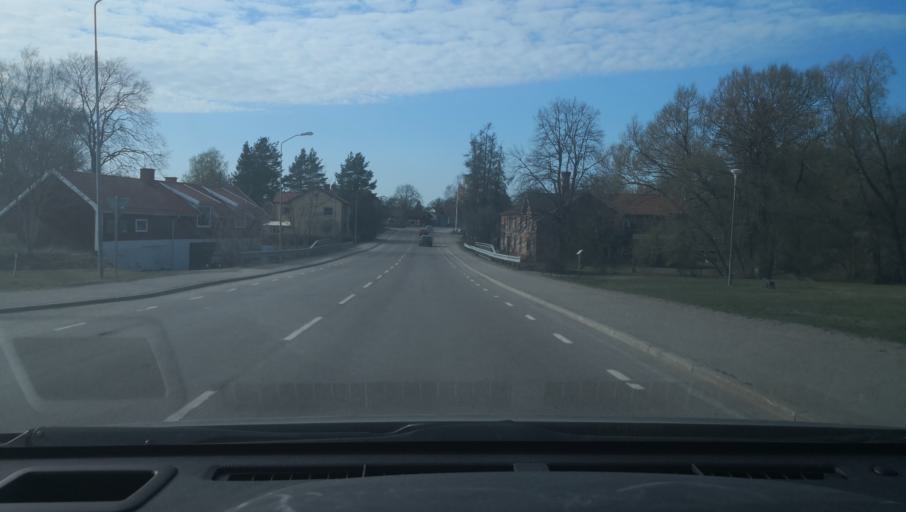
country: SE
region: Uppsala
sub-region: Heby Kommun
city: Heby
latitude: 59.9369
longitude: 16.8678
